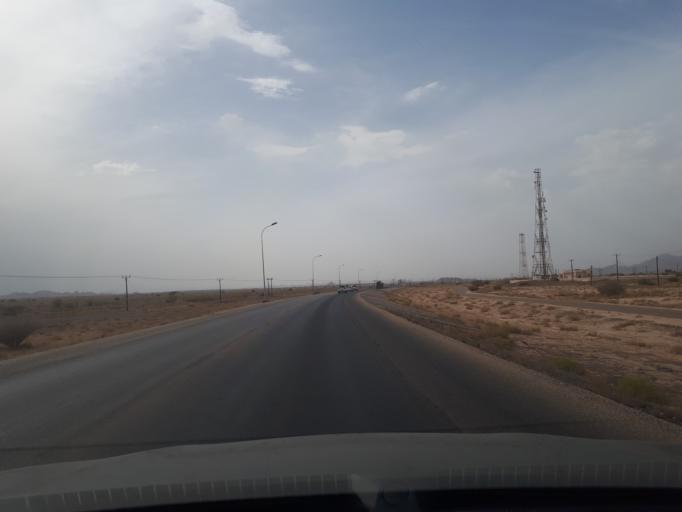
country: OM
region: Ash Sharqiyah
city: Al Qabil
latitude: 22.5100
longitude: 58.7408
